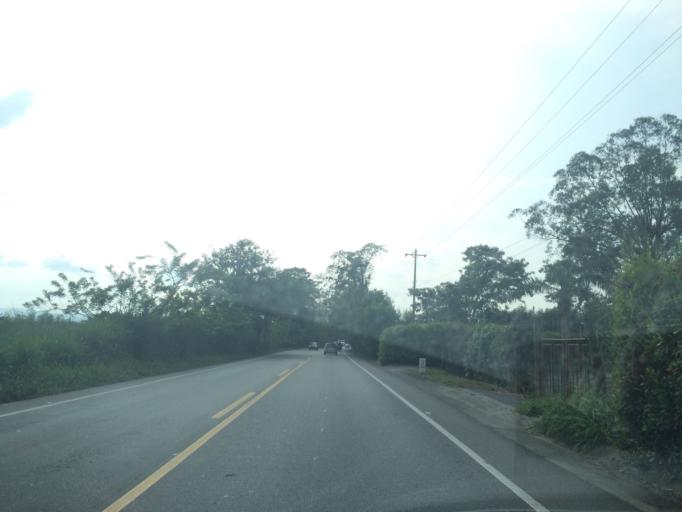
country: CO
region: Quindio
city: La Tebaida
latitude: 4.4523
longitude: -75.7997
